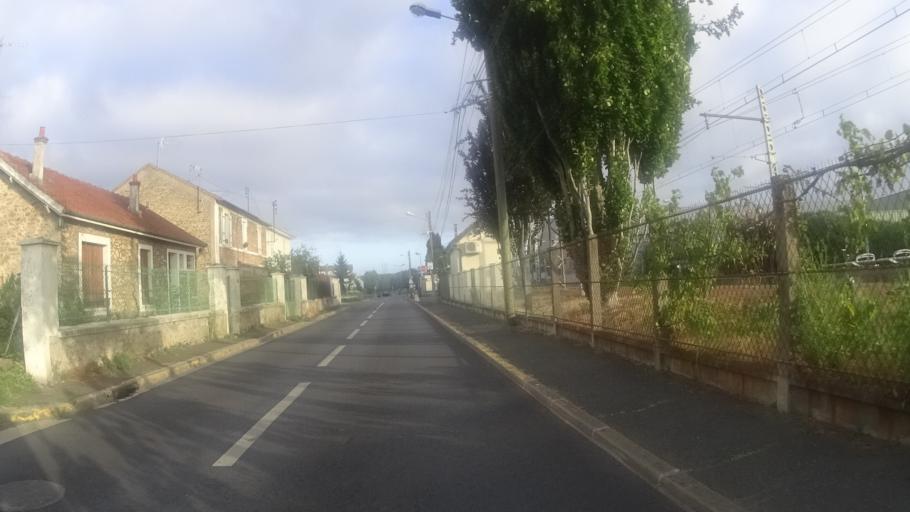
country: FR
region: Ile-de-France
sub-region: Departement de l'Essonne
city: Villabe
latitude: 48.5920
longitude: 2.4624
